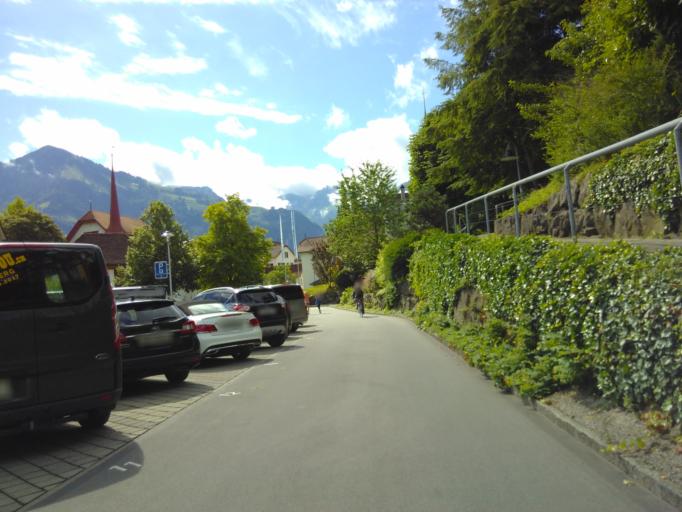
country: CH
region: Nidwalden
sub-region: Nidwalden
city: Stans
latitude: 46.9582
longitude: 8.3638
